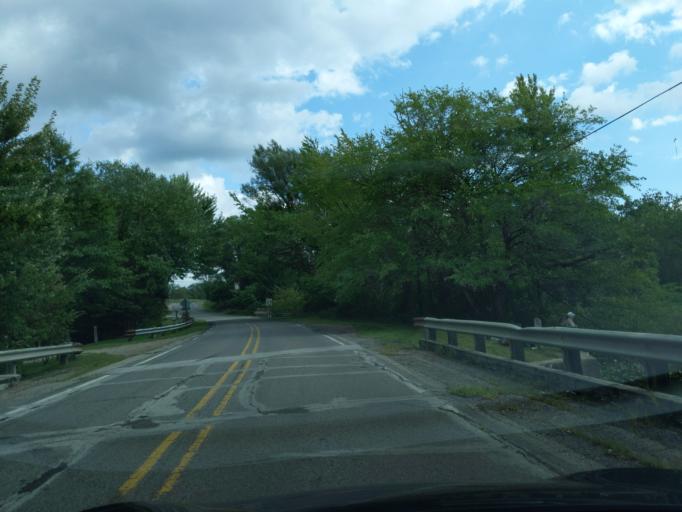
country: US
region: Michigan
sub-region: Jackson County
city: Spring Arbor
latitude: 42.3377
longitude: -84.5489
